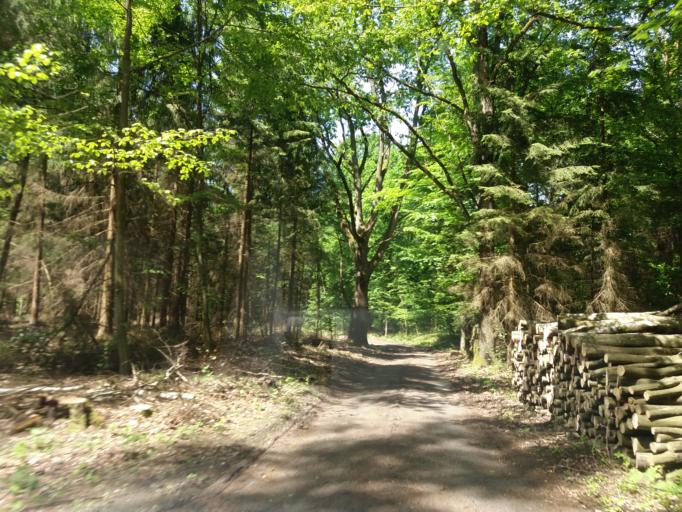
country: PL
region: West Pomeranian Voivodeship
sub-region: Powiat stargardzki
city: Dobrzany
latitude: 53.3476
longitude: 15.5130
